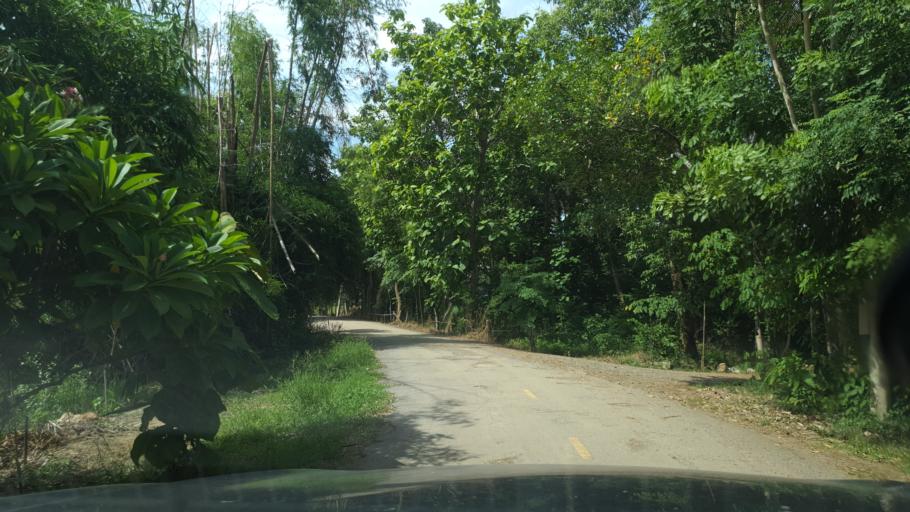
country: TH
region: Sukhothai
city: Sawankhalok
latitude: 17.2185
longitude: 99.7137
